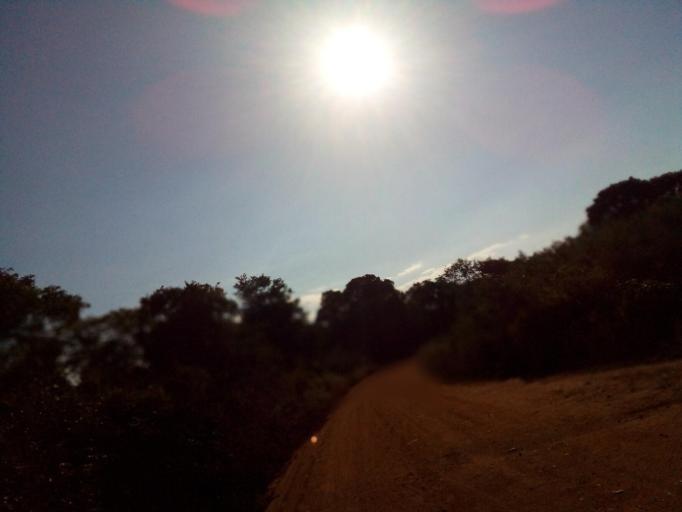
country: MZ
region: Zambezia
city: Quelimane
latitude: -17.4844
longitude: 36.5473
